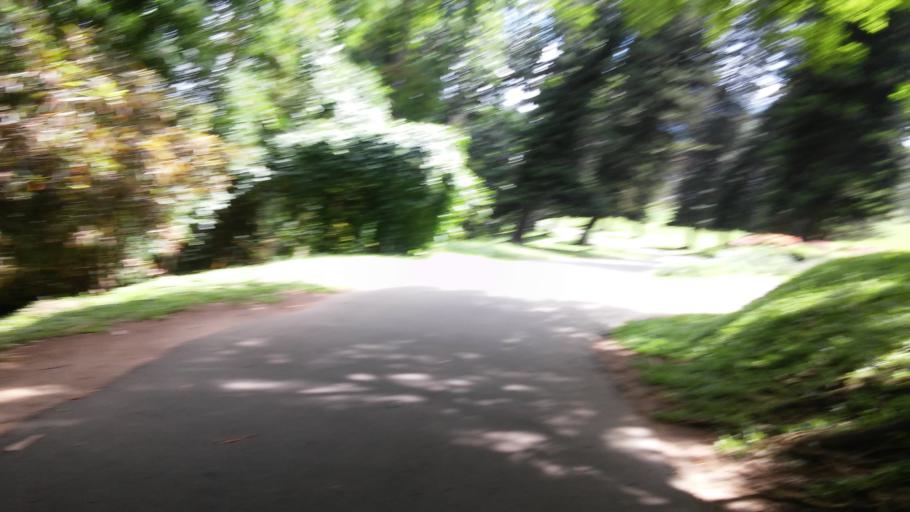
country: LK
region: Central
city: Kandy
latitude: 7.2687
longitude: 80.5939
